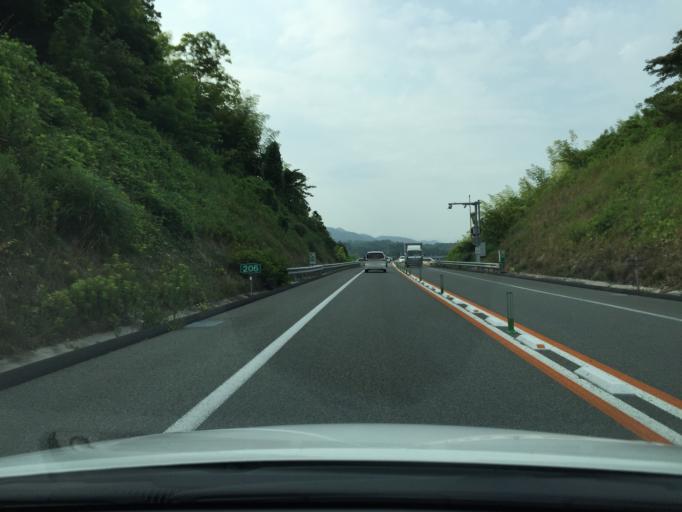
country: JP
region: Fukushima
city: Namie
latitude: 37.2704
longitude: 140.9846
